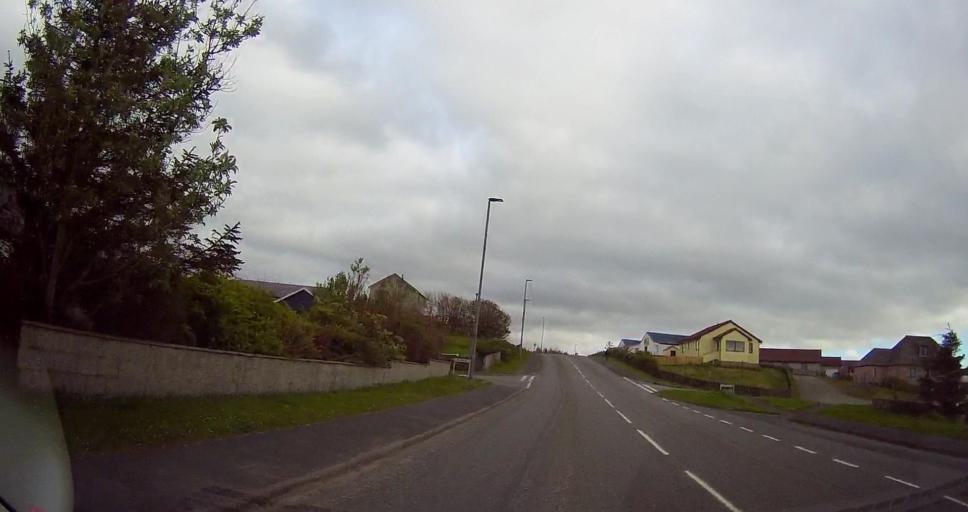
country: GB
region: Scotland
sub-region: Shetland Islands
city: Lerwick
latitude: 60.3895
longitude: -1.3487
